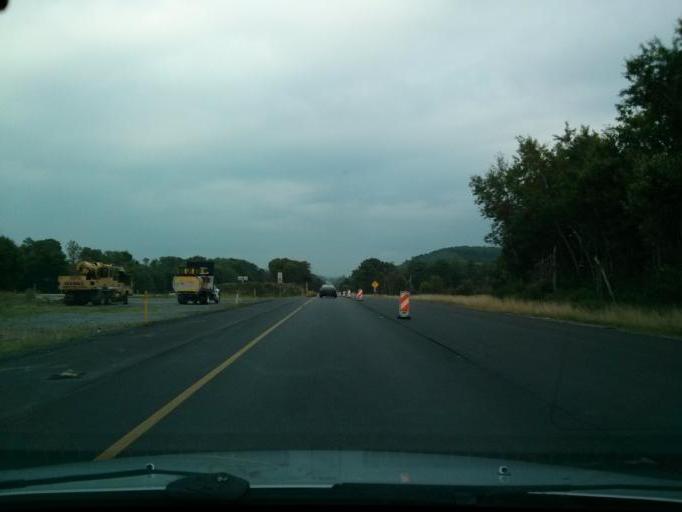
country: US
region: Pennsylvania
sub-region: Jefferson County
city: Reynoldsville
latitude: 41.1522
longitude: -78.9134
